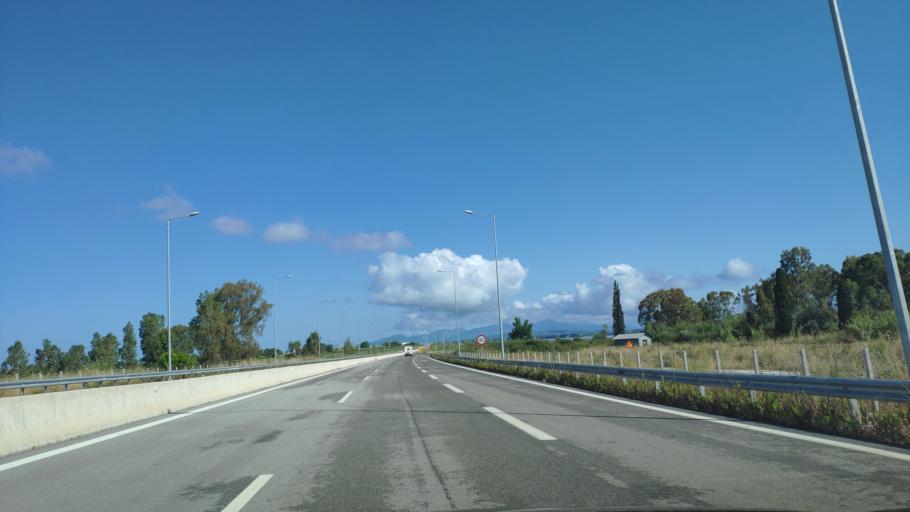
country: GR
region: Epirus
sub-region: Nomos Prevezis
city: Preveza
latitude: 38.9178
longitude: 20.7909
